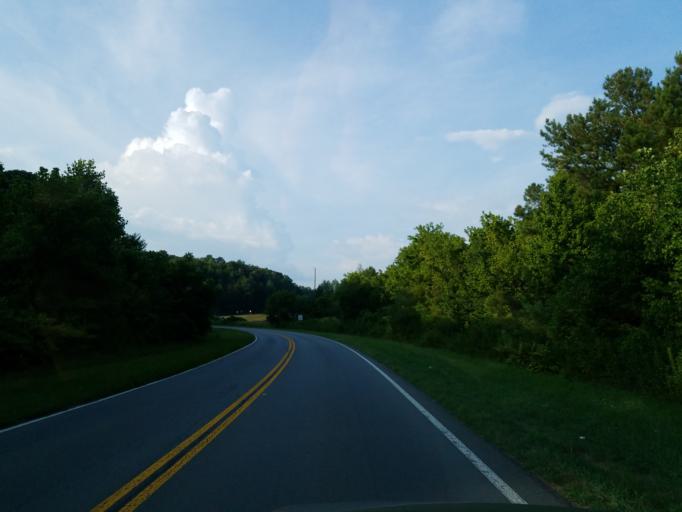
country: US
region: Georgia
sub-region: Gilmer County
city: Ellijay
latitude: 34.6184
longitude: -84.5188
